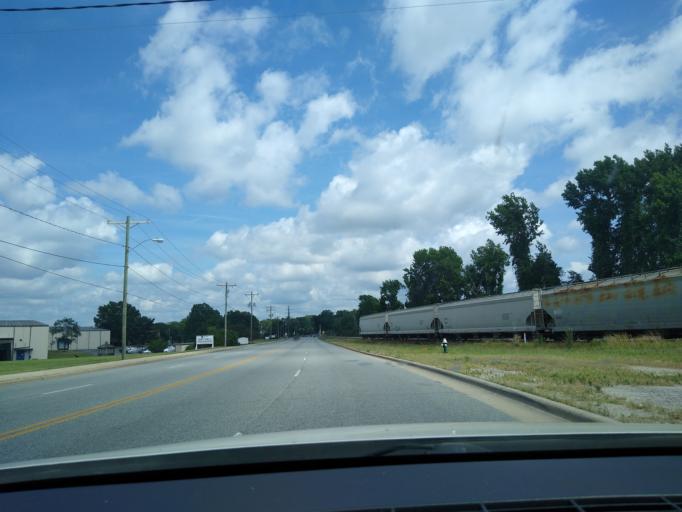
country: US
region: North Carolina
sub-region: Guilford County
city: Greensboro
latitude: 36.0637
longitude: -79.8645
